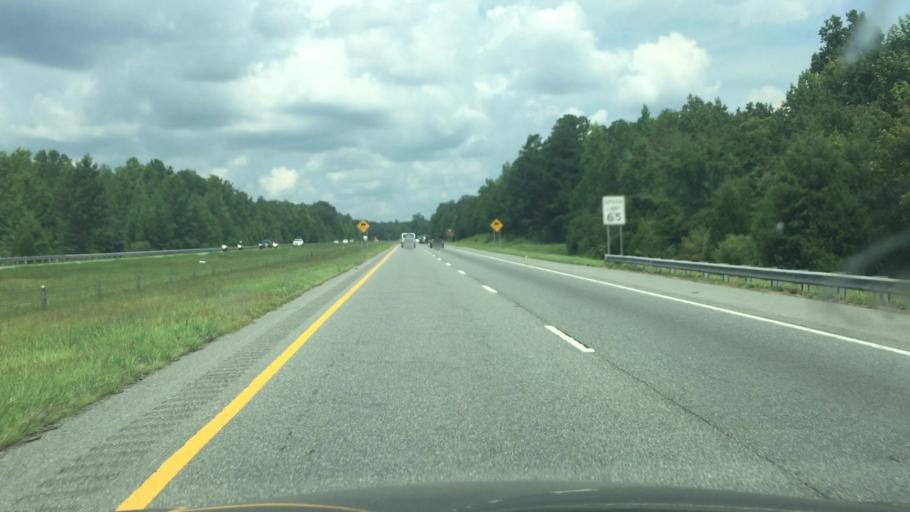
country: US
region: North Carolina
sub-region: Randolph County
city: Asheboro
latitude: 35.5757
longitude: -79.8060
